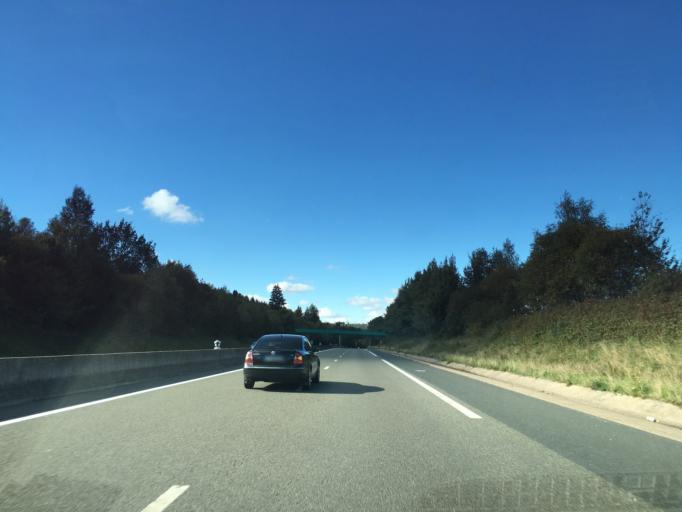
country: FR
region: Lorraine
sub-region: Departement des Vosges
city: Etival-Clairefontaine
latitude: 48.4081
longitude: 6.8085
